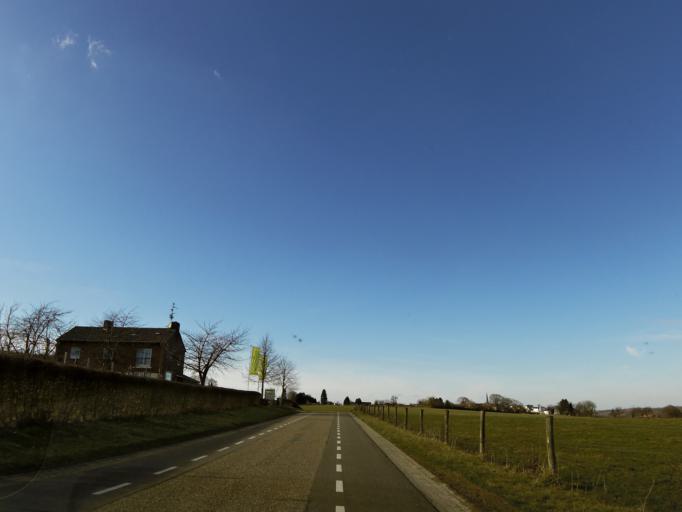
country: NL
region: Limburg
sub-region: Gemeente Vaals
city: Vaals
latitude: 50.7698
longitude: 5.9929
